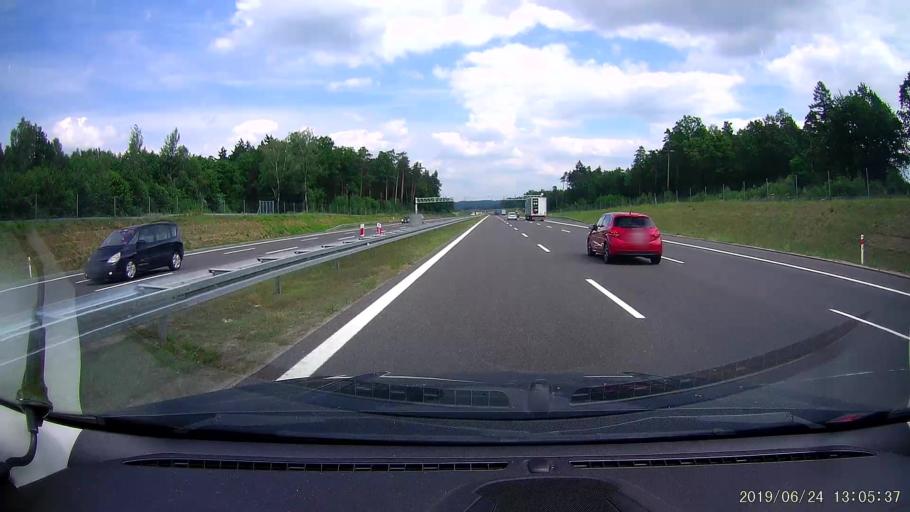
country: PL
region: Silesian Voivodeship
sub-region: Powiat rybnicki
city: Stanowice
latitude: 50.1102
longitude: 18.6753
